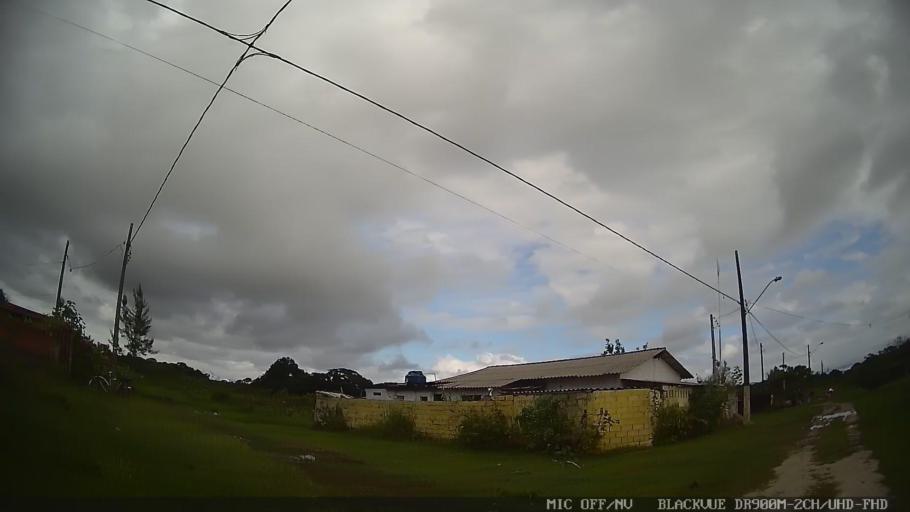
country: BR
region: Sao Paulo
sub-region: Itanhaem
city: Itanhaem
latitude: -24.2184
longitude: -46.8818
